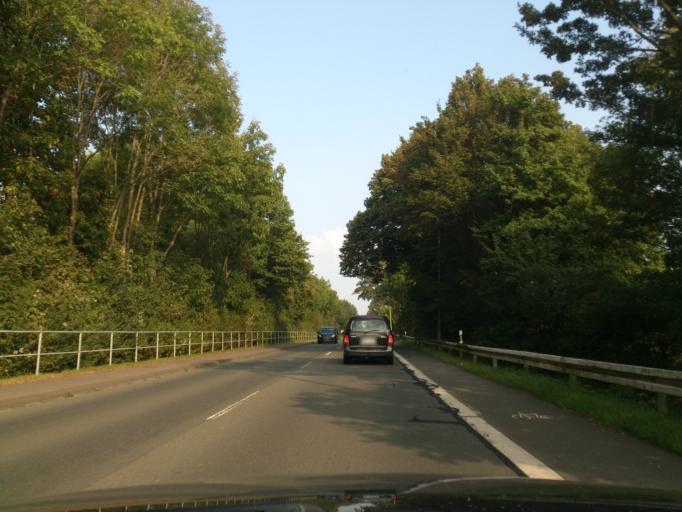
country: DE
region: North Rhine-Westphalia
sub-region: Regierungsbezirk Detmold
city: Paderborn
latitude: 51.7183
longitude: 8.7882
